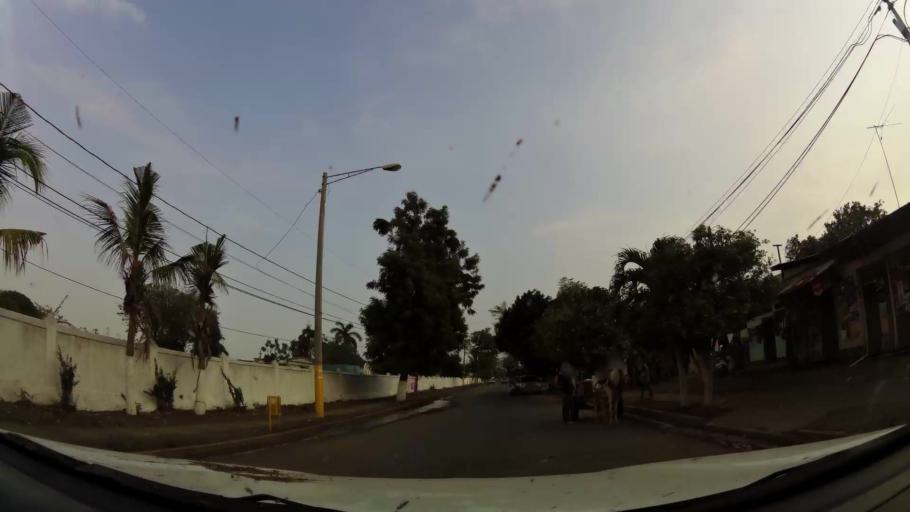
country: NI
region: Masaya
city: Masaya
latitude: 11.9853
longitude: -86.1038
